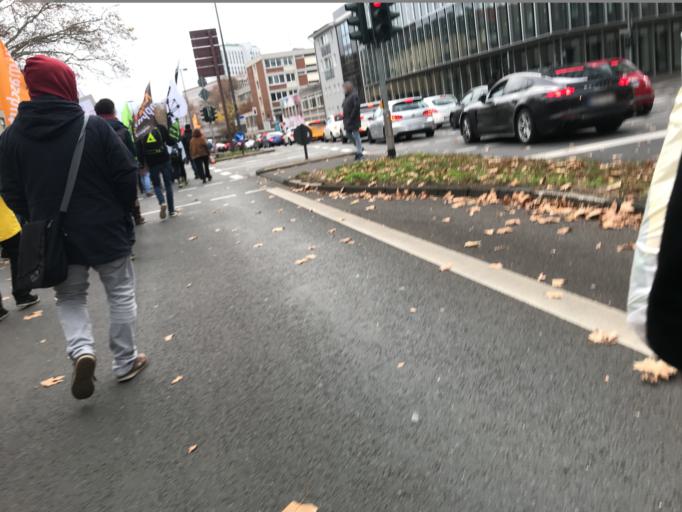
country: DE
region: North Rhine-Westphalia
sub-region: Regierungsbezirk Koln
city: Koeln
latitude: 50.9337
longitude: 6.9533
